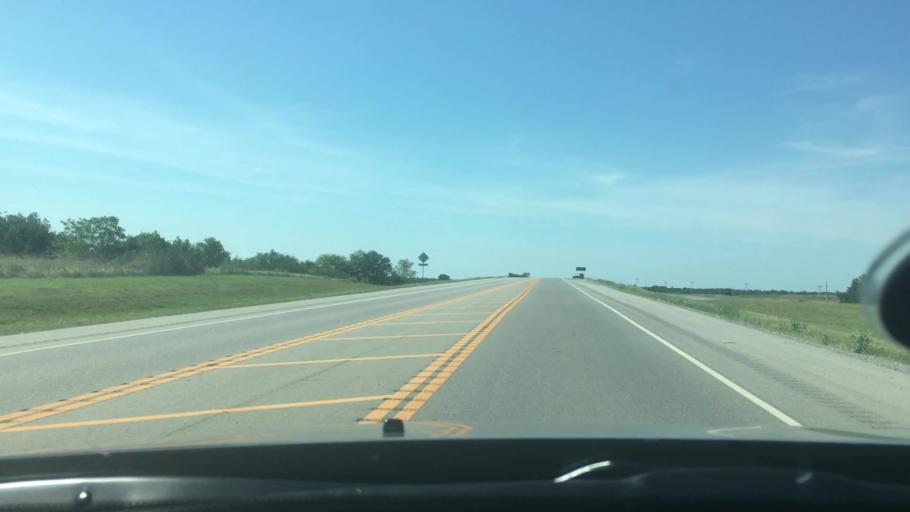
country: US
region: Oklahoma
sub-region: Bryan County
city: Durant
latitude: 33.9892
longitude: -96.3397
